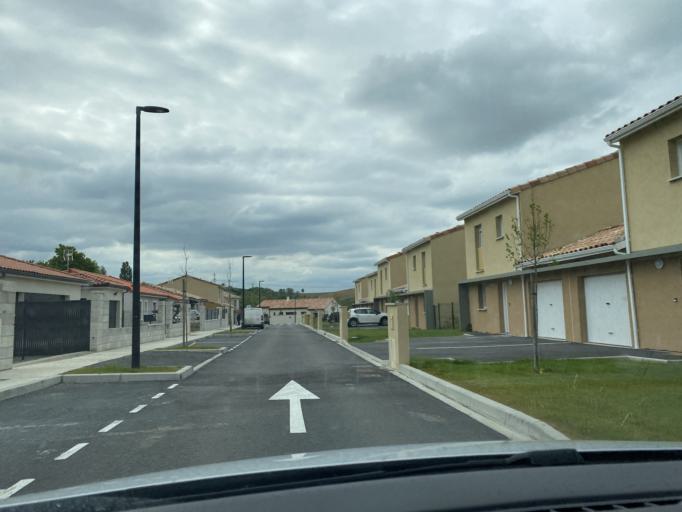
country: FR
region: Midi-Pyrenees
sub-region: Departement de la Haute-Garonne
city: Ayguesvives
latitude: 43.4282
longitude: 1.5942
